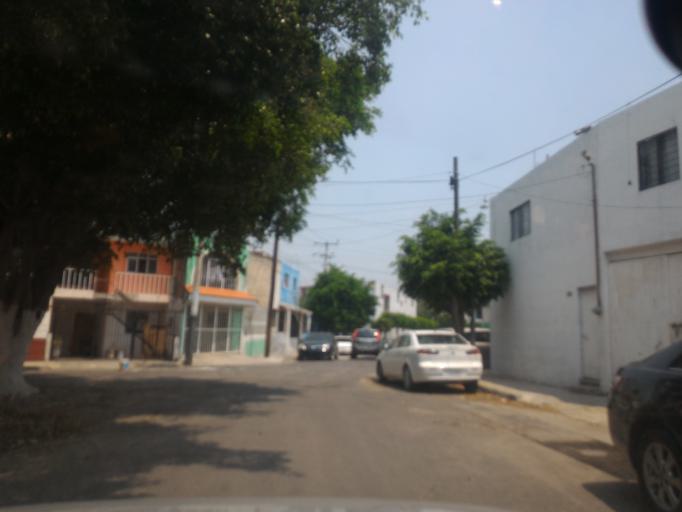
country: MX
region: Jalisco
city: Guadalajara
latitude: 20.6271
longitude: -103.3835
